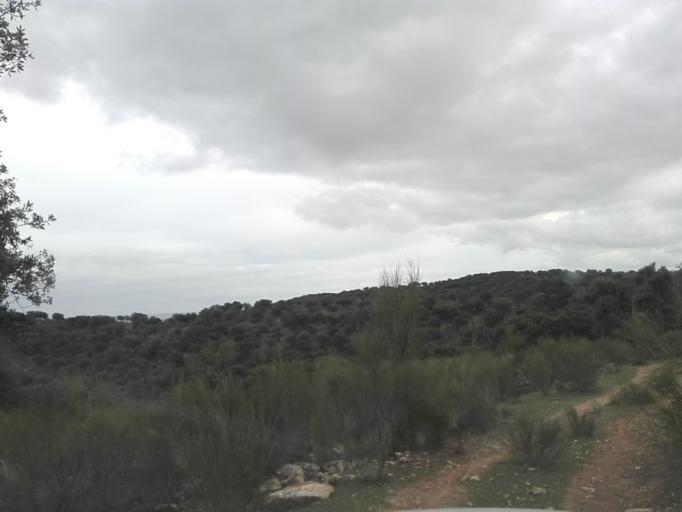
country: ES
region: Extremadura
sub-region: Provincia de Badajoz
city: Hinojosa del Valle
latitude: 38.4396
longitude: -6.1937
